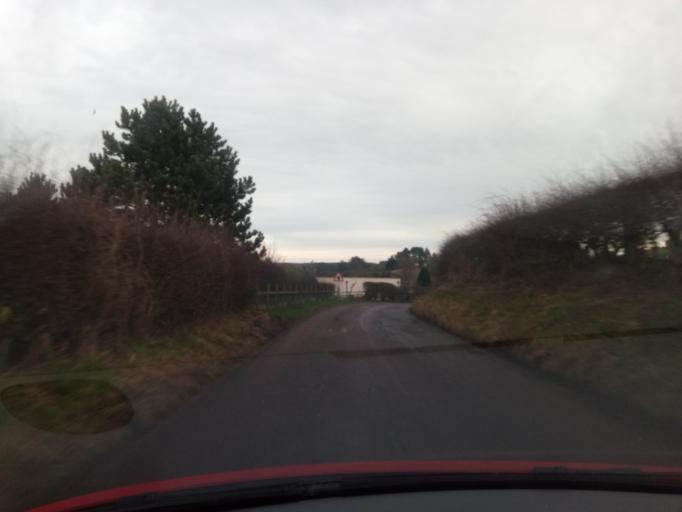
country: GB
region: England
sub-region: Northumberland
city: Wooler
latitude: 55.5512
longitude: -2.0293
